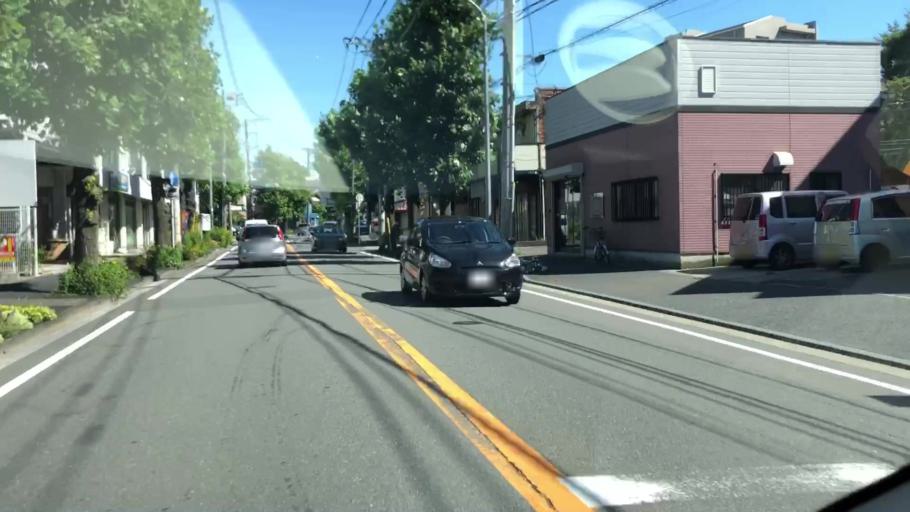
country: JP
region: Kanagawa
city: Yokohama
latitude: 35.3840
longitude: 139.6037
